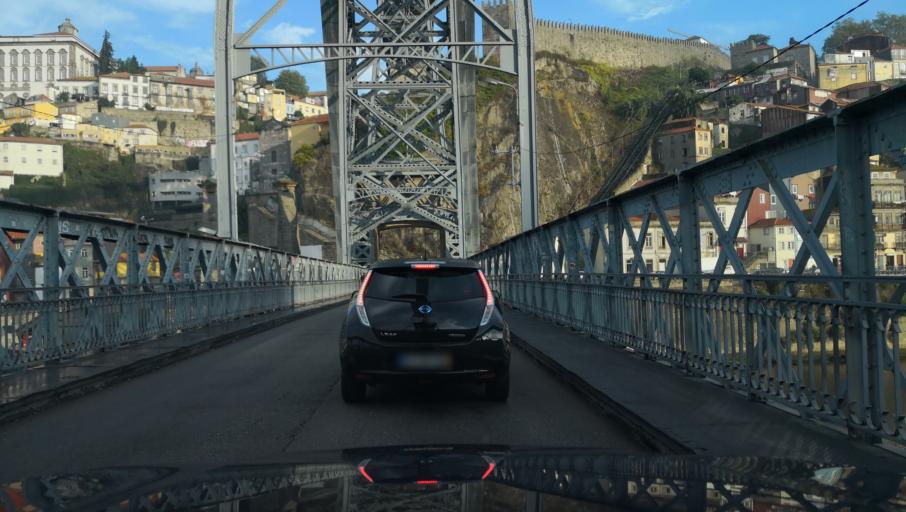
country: PT
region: Porto
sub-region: Porto
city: Porto
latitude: 41.1399
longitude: -8.6094
